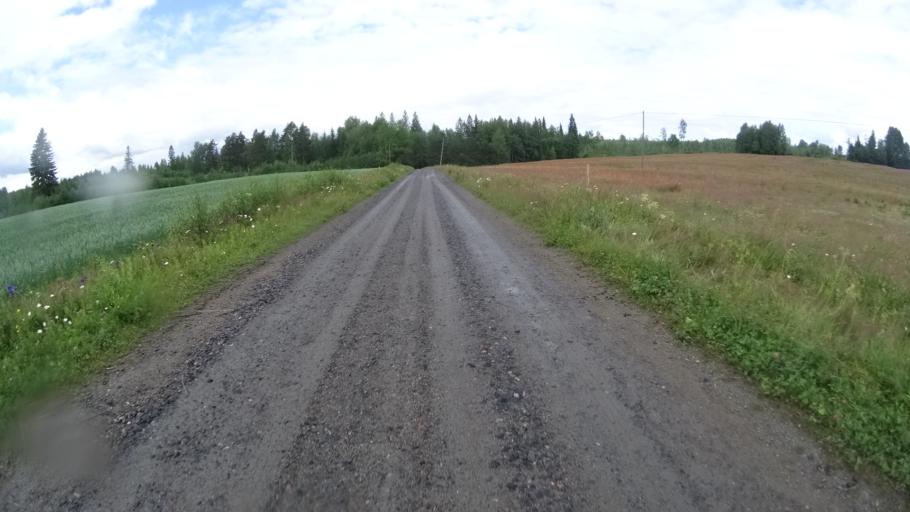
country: FI
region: Uusimaa
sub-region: Helsinki
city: Karkkila
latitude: 60.5865
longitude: 24.3400
